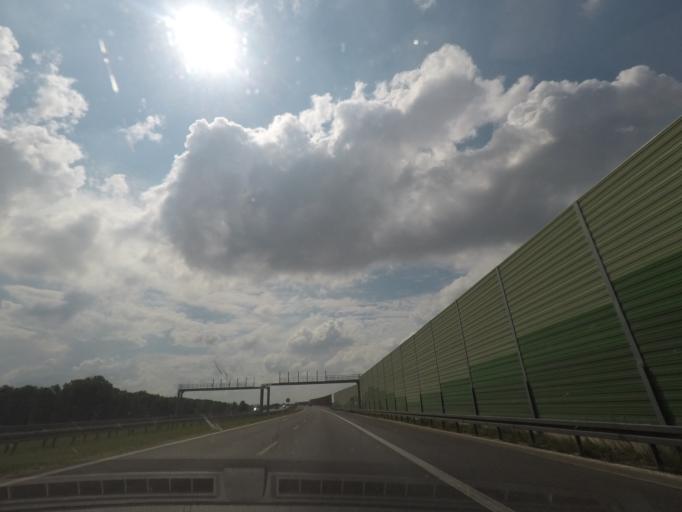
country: PL
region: Lodz Voivodeship
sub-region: Powiat kutnowski
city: Krzyzanow
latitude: 52.1432
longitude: 19.4822
